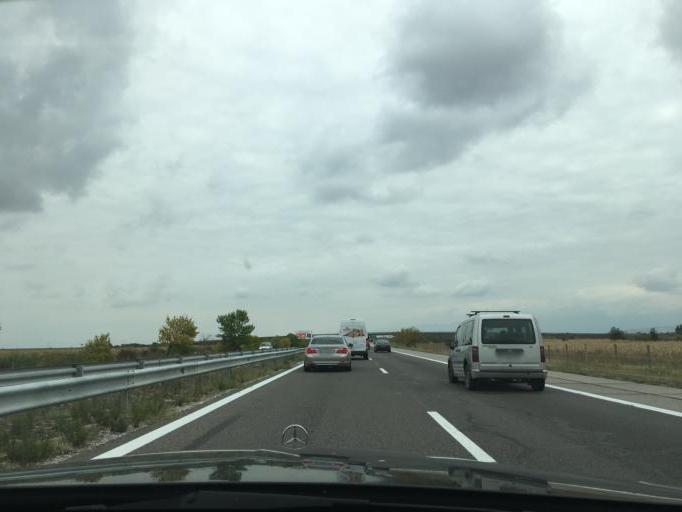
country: BG
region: Pazardzhik
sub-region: Obshtina Pazardzhik
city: Pazardzhik
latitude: 42.2471
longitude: 24.3515
